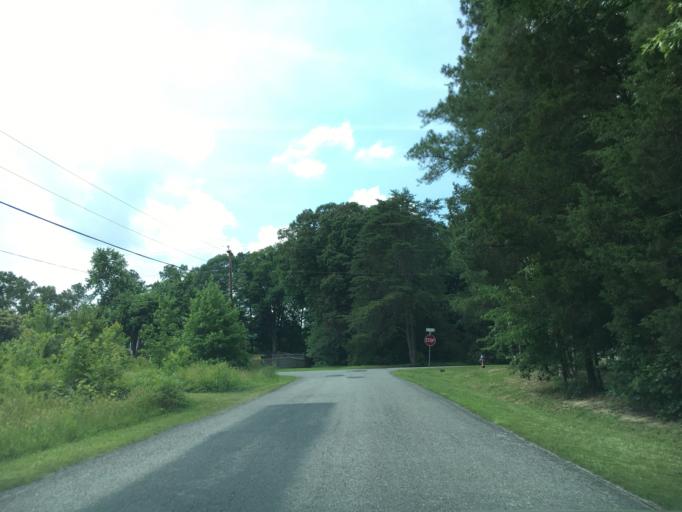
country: US
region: Virginia
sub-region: Henrico County
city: Short Pump
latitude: 37.6678
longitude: -77.6611
